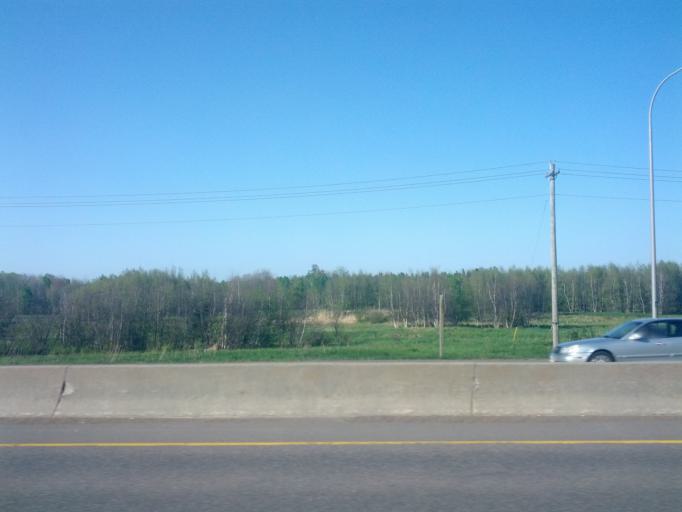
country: CA
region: New Brunswick
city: Moncton
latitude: 46.1067
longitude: -64.7982
